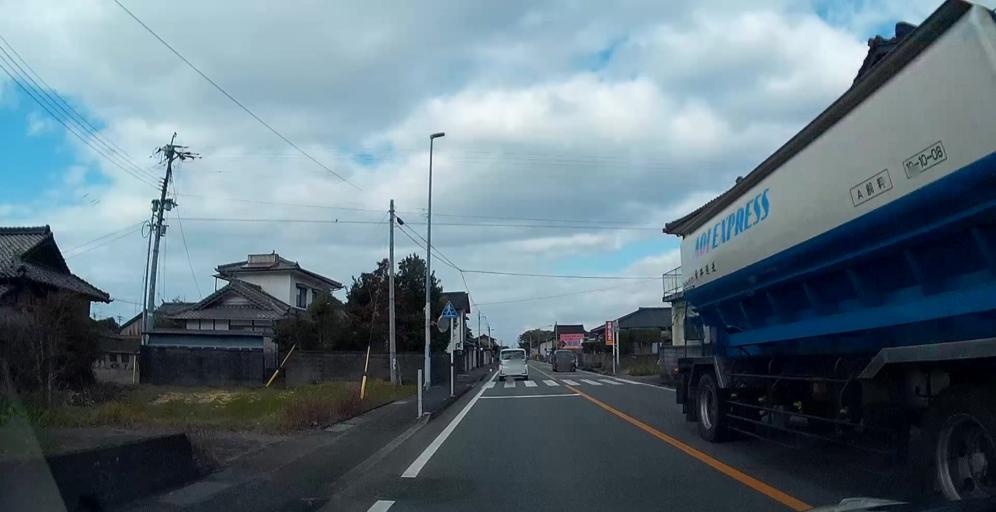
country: JP
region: Kumamoto
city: Yatsushiro
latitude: 32.4419
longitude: 130.5860
